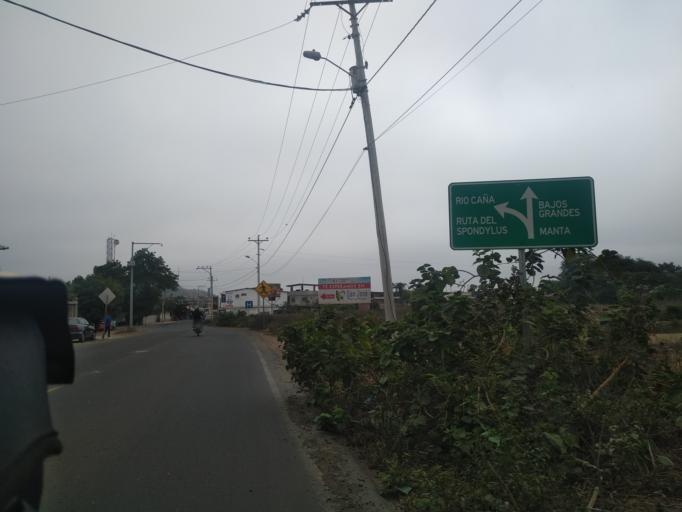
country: EC
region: Manabi
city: Montecristi
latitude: -1.0819
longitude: -80.6784
